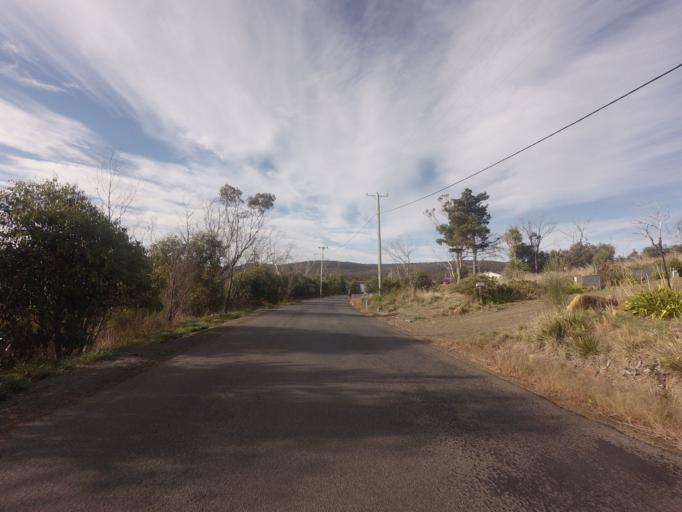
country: AU
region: Tasmania
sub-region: Sorell
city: Sorell
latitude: -42.9468
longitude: 147.8535
